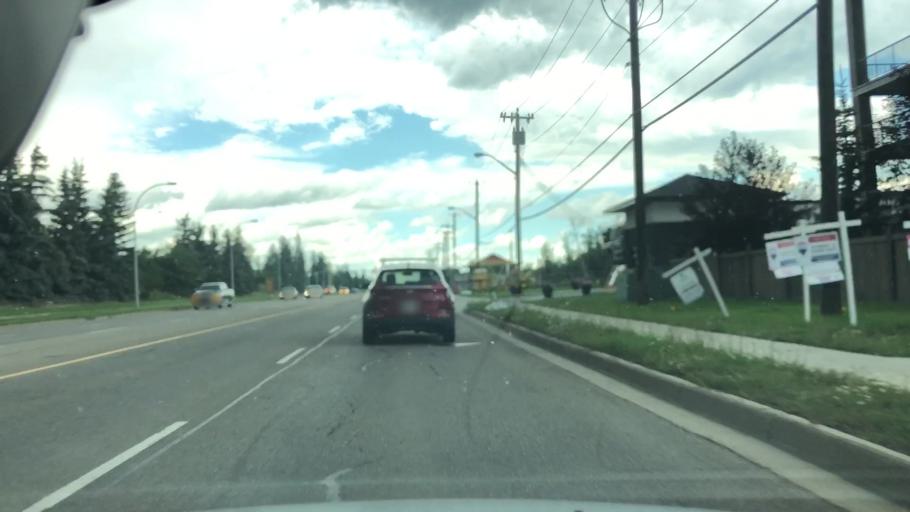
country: CA
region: Alberta
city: Edmonton
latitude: 53.6082
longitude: -113.5412
